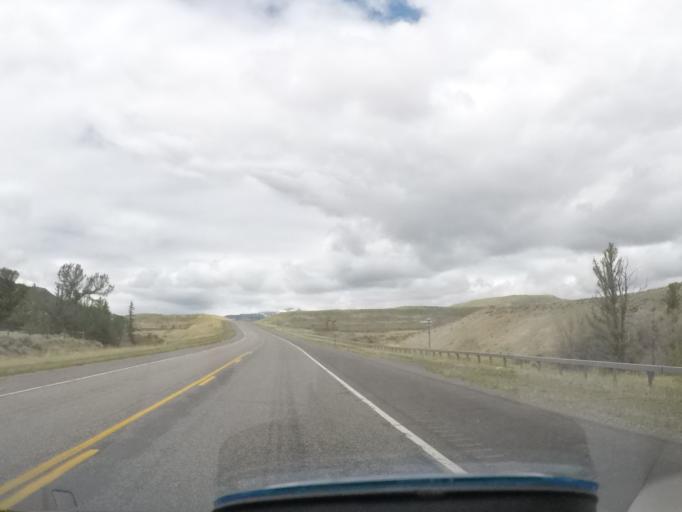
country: US
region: Wyoming
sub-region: Sublette County
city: Pinedale
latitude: 43.5825
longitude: -109.7655
